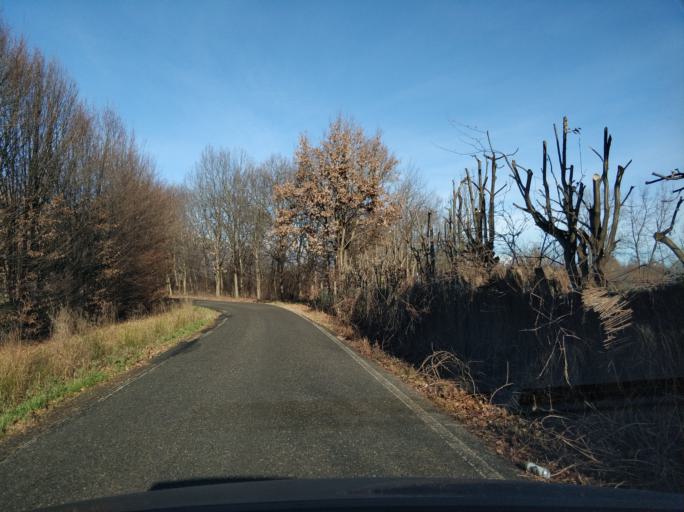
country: IT
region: Piedmont
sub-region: Provincia di Torino
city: Fiano
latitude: 45.2157
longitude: 7.5478
